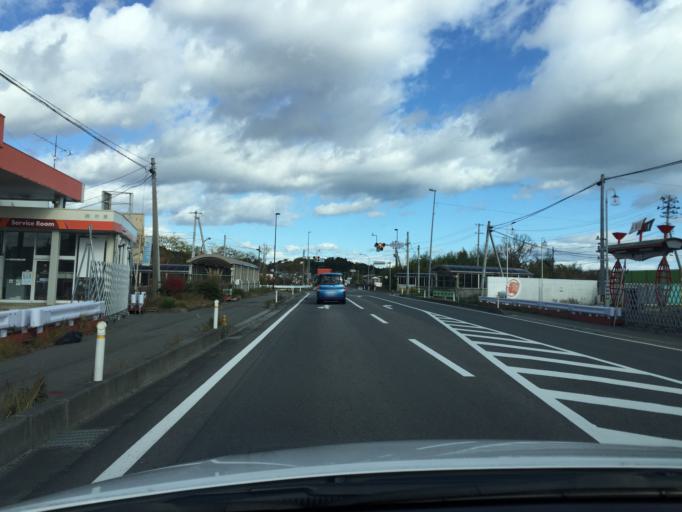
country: JP
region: Fukushima
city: Namie
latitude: 37.4525
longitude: 141.0094
